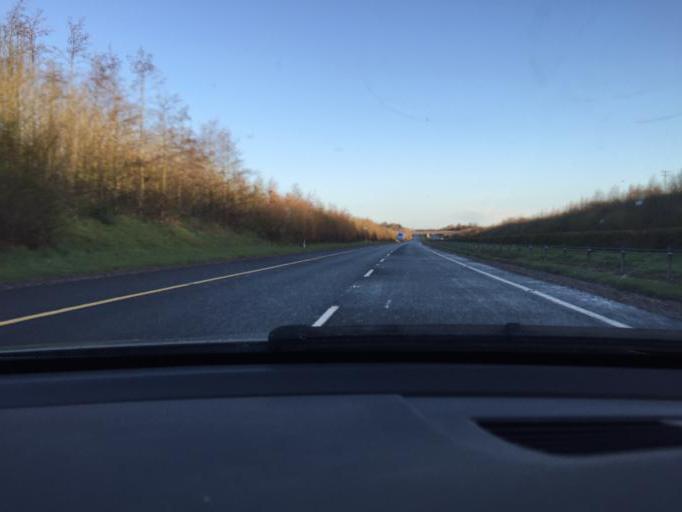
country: IE
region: Leinster
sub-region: Lu
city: Drogheda
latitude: 53.6806
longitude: -6.3606
